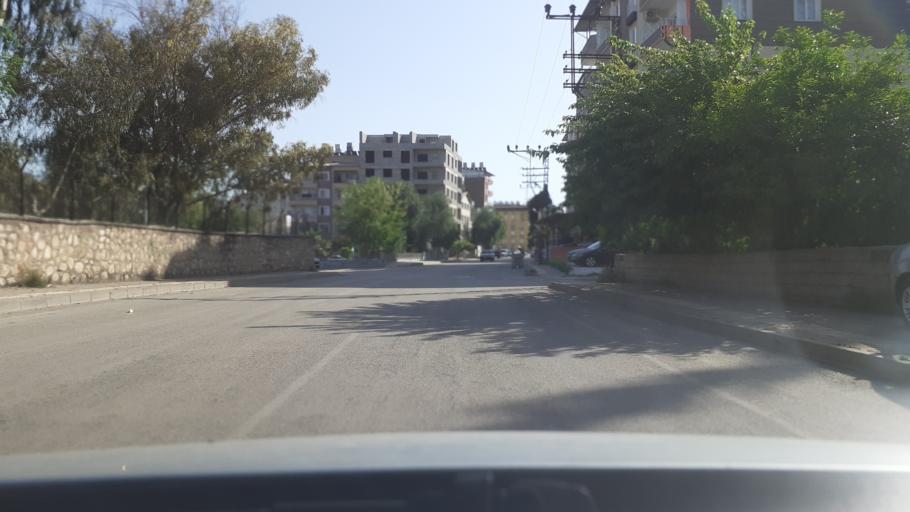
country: TR
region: Hatay
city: Kirikhan
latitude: 36.4932
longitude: 36.3670
